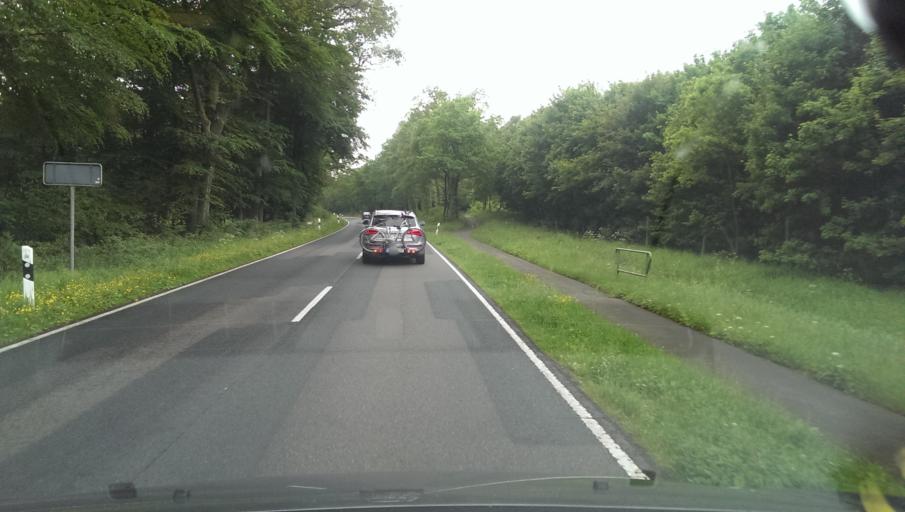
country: DE
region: Lower Saxony
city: Unterluss
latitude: 52.8683
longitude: 10.2464
